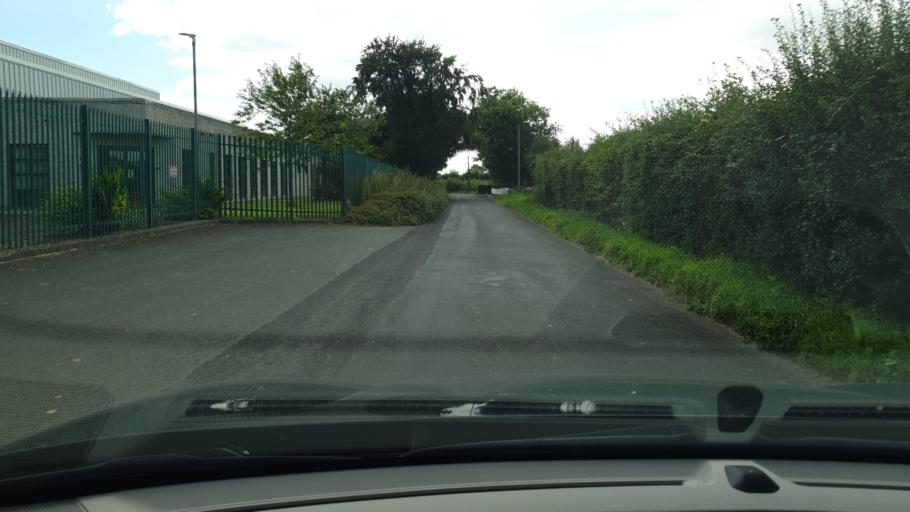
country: IE
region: Leinster
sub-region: An Mhi
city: Dunboyne
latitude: 53.4080
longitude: -6.4906
